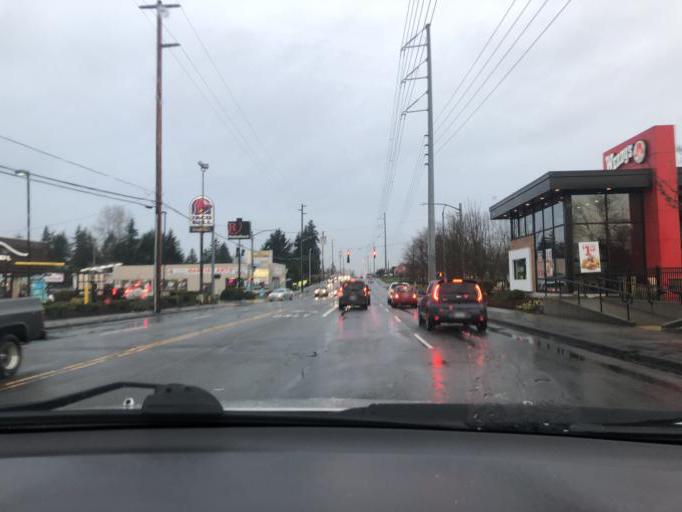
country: US
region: Washington
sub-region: Pierce County
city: Midland
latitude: 47.1918
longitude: -122.4095
